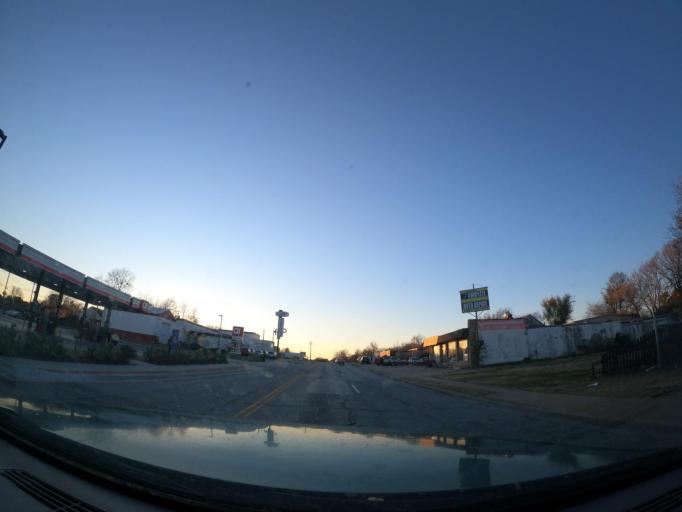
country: US
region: Oklahoma
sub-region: Tulsa County
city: Tulsa
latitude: 36.1608
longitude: -95.9412
